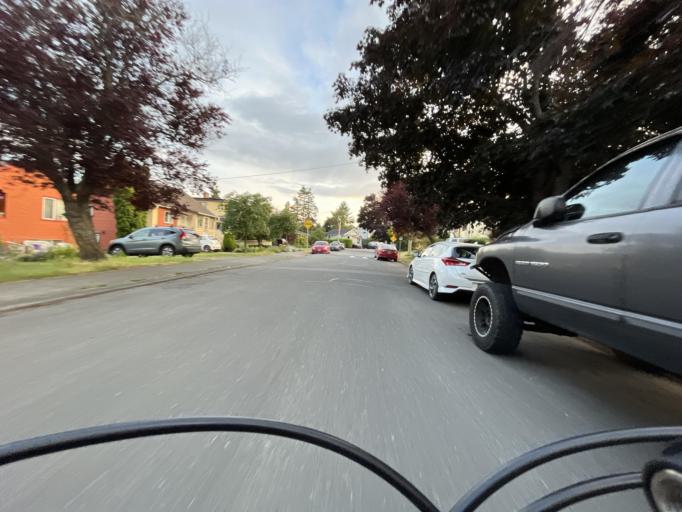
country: CA
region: British Columbia
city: Victoria
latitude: 48.4287
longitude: -123.4021
